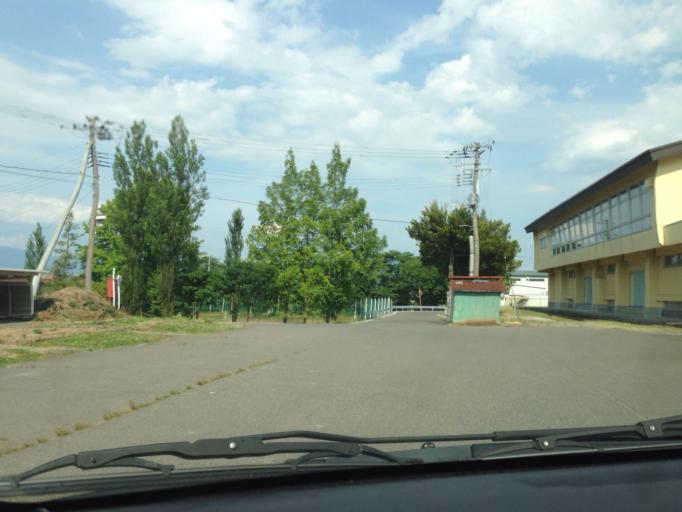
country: JP
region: Fukushima
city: Kitakata
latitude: 37.5137
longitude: 139.8307
